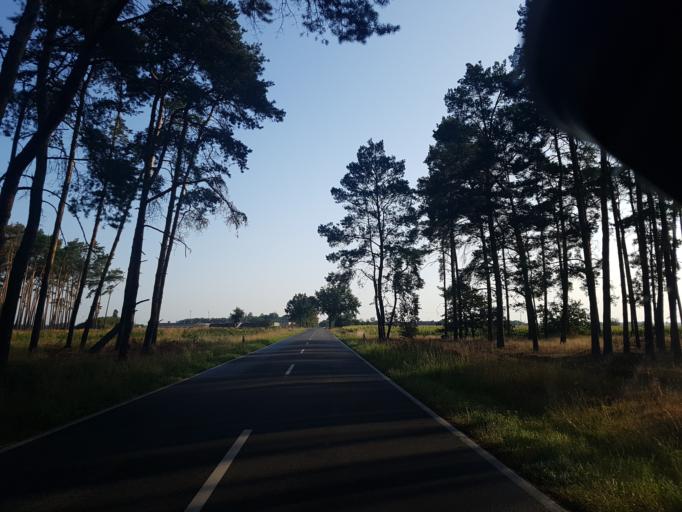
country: DE
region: Saxony-Anhalt
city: Holzdorf
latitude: 51.8066
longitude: 13.1396
